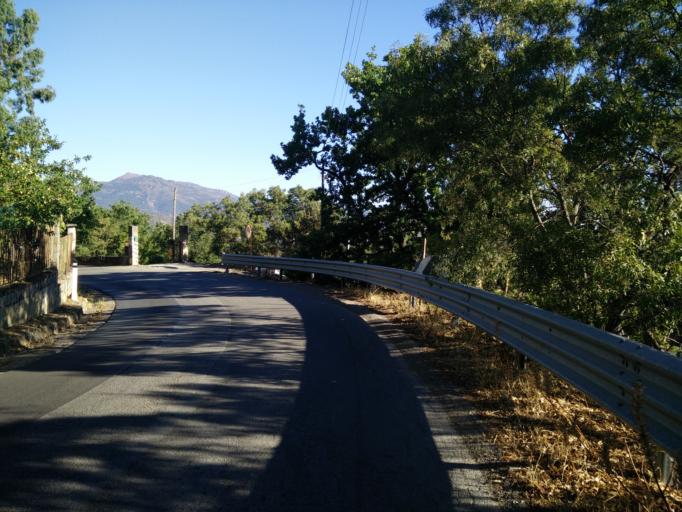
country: IT
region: Sicily
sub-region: Palermo
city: Castelbuono
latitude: 37.9209
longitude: 14.0920
